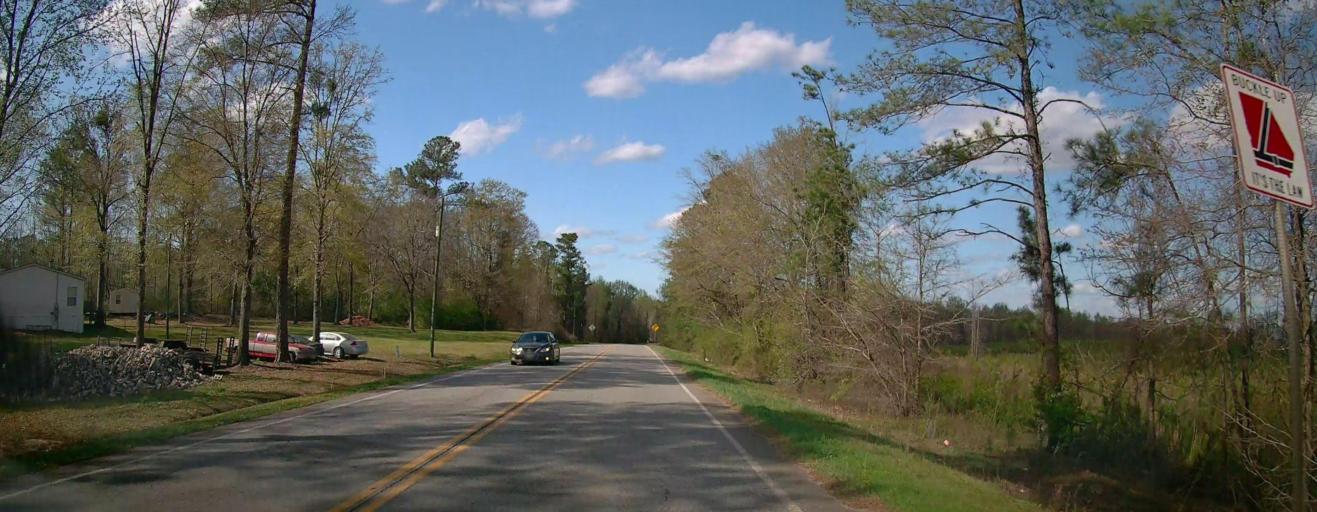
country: US
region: Georgia
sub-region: Wilkinson County
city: Gordon
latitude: 32.9588
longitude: -83.2900
